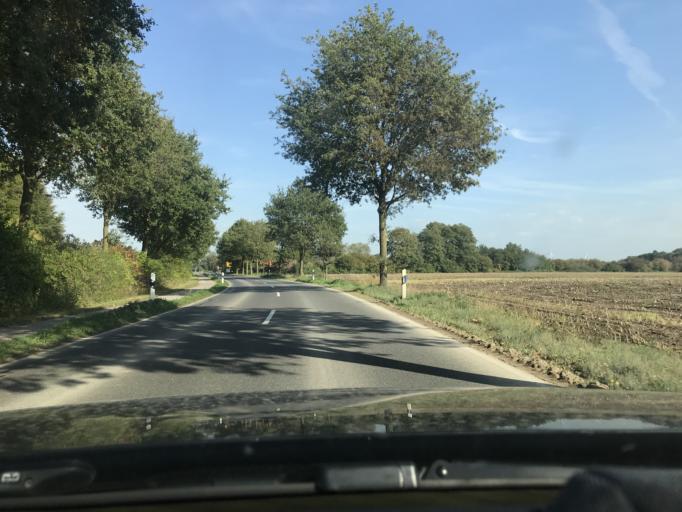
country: DE
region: North Rhine-Westphalia
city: Kalkar
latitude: 51.7439
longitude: 6.2592
